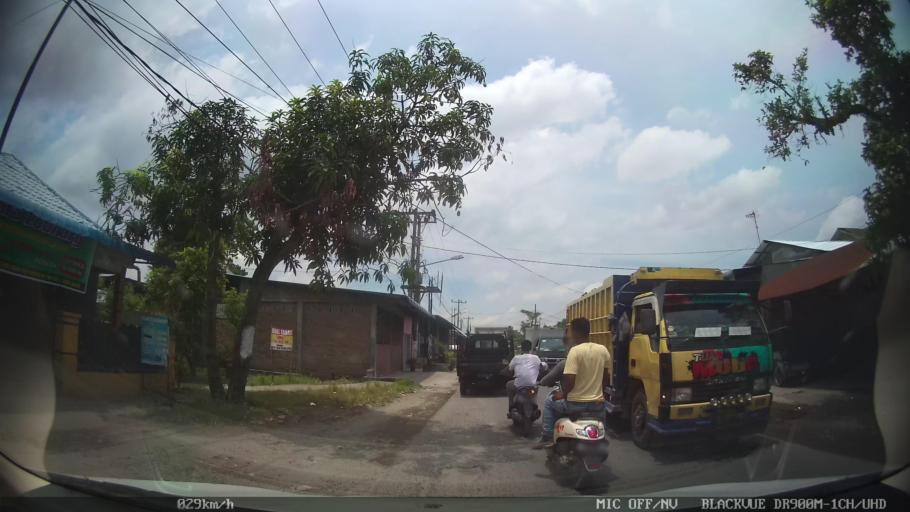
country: ID
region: North Sumatra
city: Labuhan Deli
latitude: 3.6808
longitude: 98.6702
